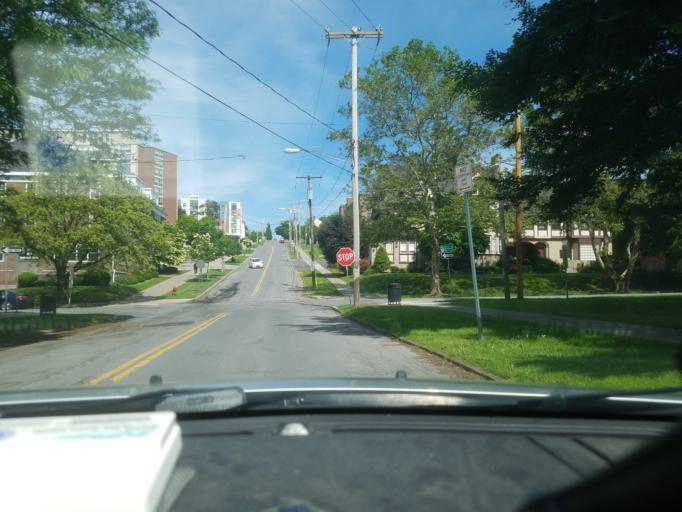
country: US
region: New York
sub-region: Onondaga County
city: Syracuse
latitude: 43.0415
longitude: -76.1327
